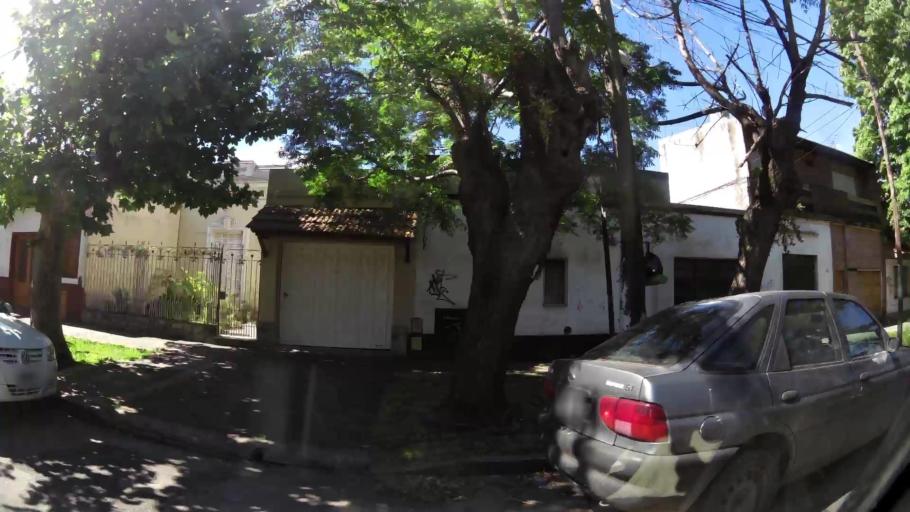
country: AR
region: Buenos Aires
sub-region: Partido de Lomas de Zamora
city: Lomas de Zamora
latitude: -34.7615
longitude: -58.4113
